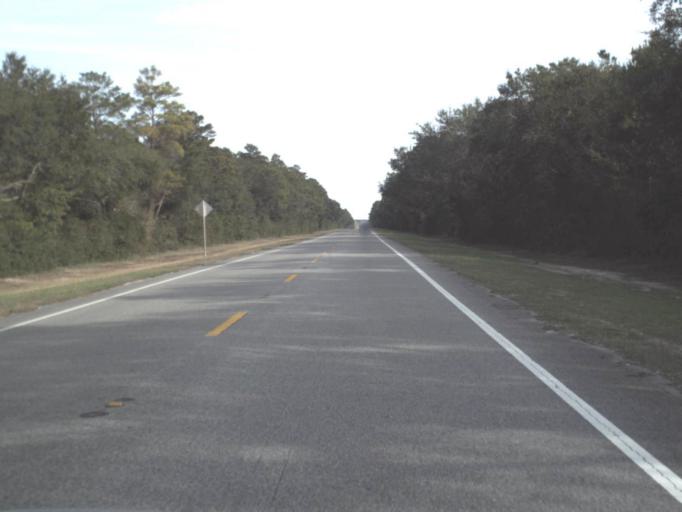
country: US
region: Florida
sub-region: Bay County
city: Mexico Beach
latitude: 29.9622
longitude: -85.4423
